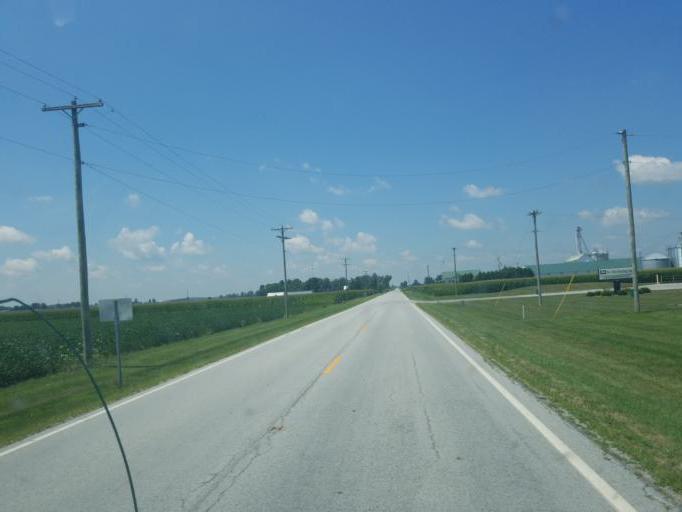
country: US
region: Ohio
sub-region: Allen County
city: Spencerville
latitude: 40.7142
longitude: -84.3620
